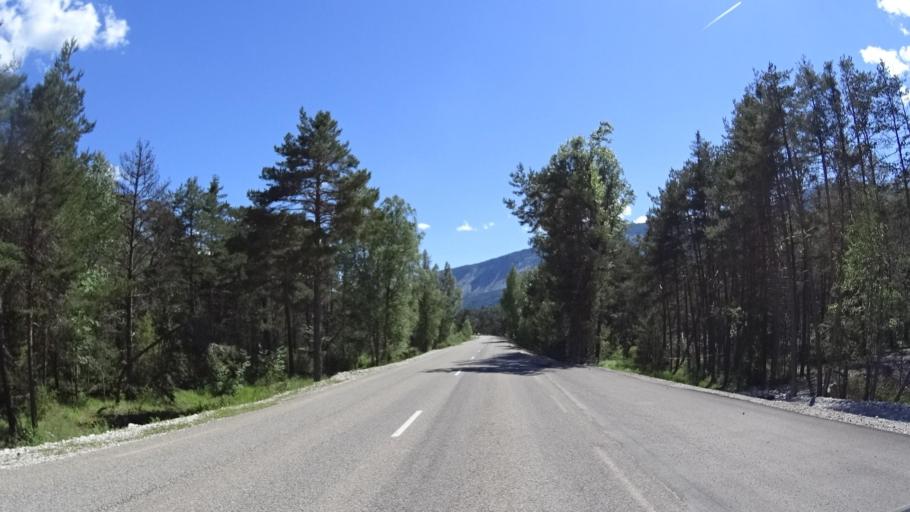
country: FR
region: Provence-Alpes-Cote d'Azur
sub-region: Departement des Alpes-de-Haute-Provence
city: Annot
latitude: 44.1568
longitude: 6.6011
